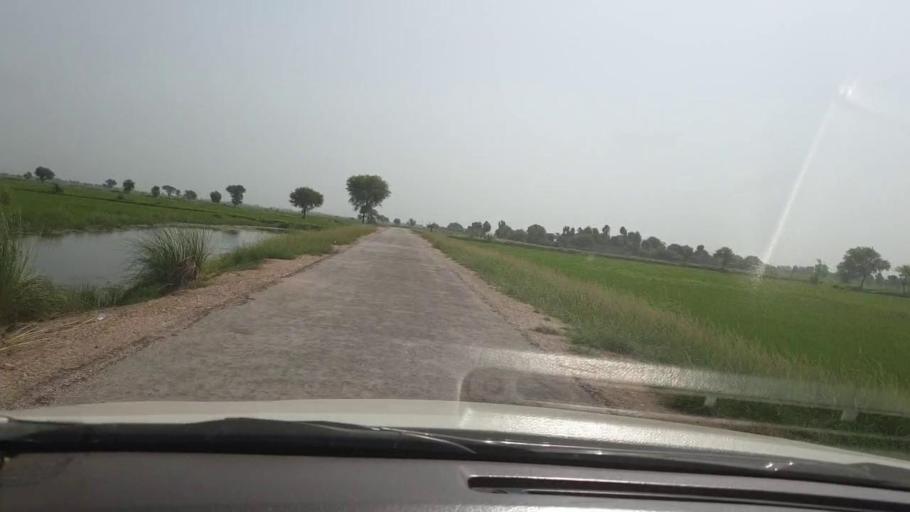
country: PK
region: Sindh
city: Rustam jo Goth
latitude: 27.9766
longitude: 68.7920
